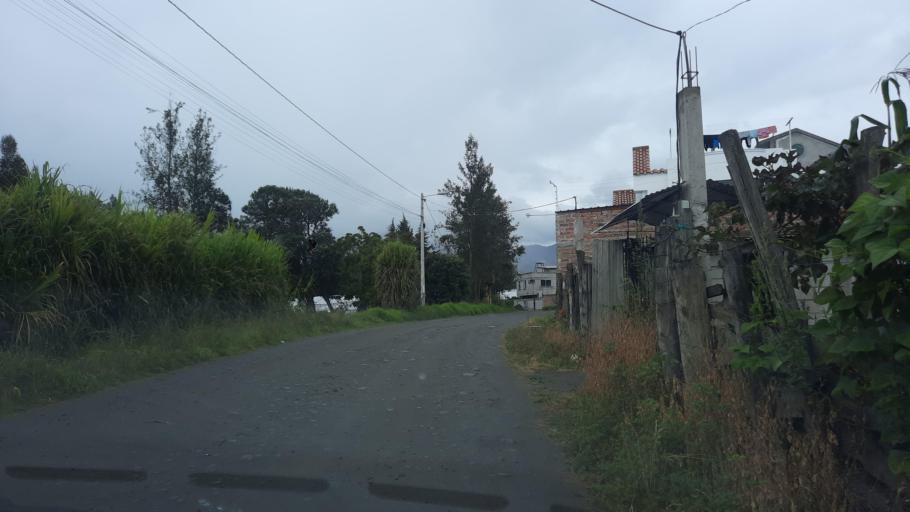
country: EC
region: Chimborazo
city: Riobamba
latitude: -1.6899
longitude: -78.6588
